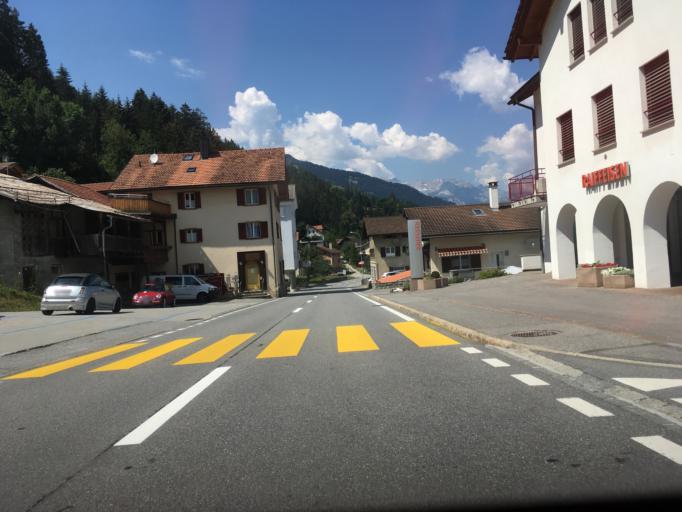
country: CH
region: Grisons
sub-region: Hinterrhein District
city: Cazis
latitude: 46.7227
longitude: 9.4283
